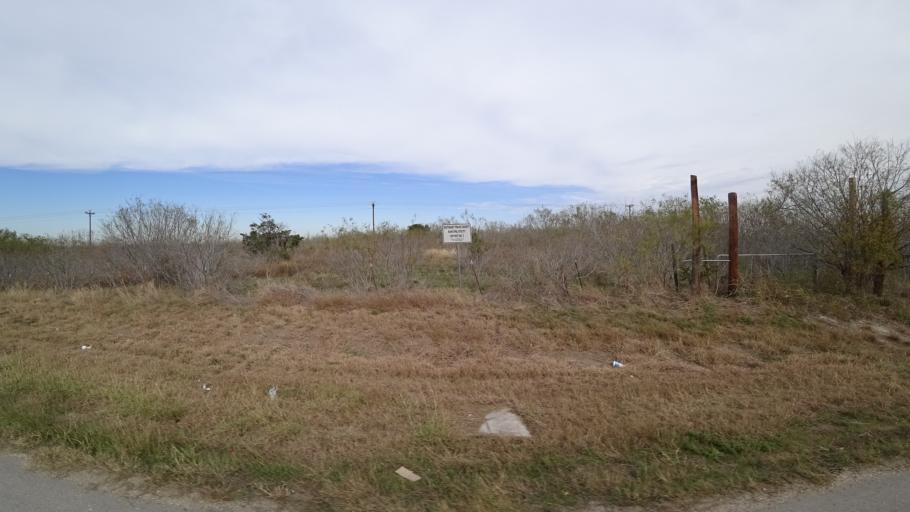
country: US
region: Texas
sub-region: Travis County
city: Garfield
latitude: 30.1465
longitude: -97.5770
